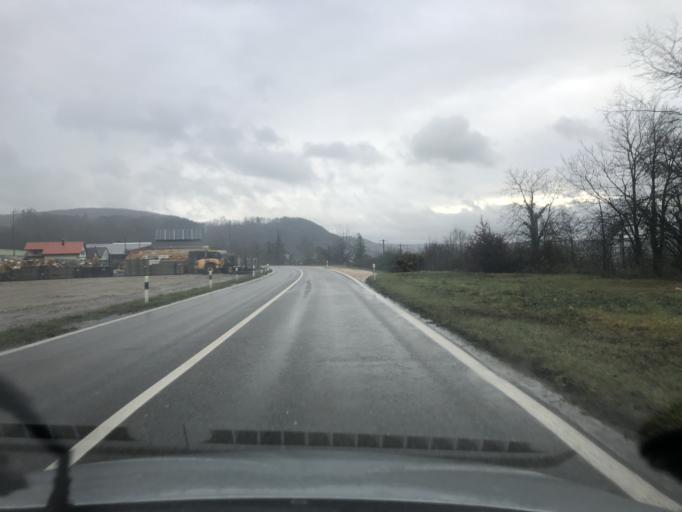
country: CH
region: Aargau
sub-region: Bezirk Zurzach
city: Koblenz
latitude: 47.5959
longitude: 8.2310
